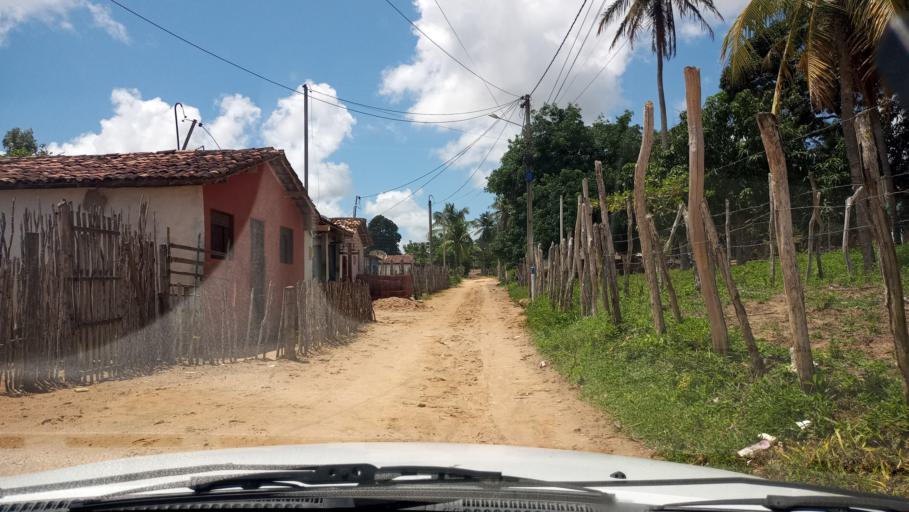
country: BR
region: Rio Grande do Norte
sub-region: Goianinha
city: Goianinha
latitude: -6.2988
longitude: -35.2207
